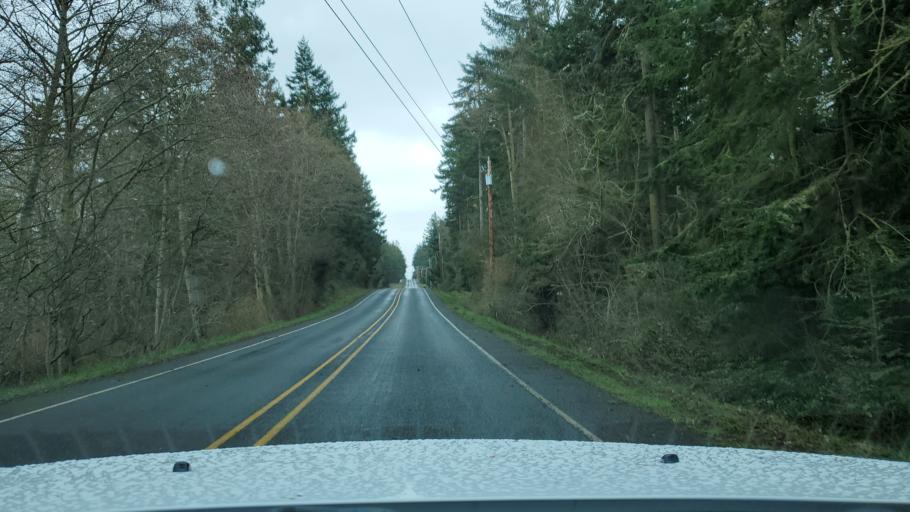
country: US
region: Washington
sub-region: Island County
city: Coupeville
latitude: 48.2318
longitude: -122.7602
